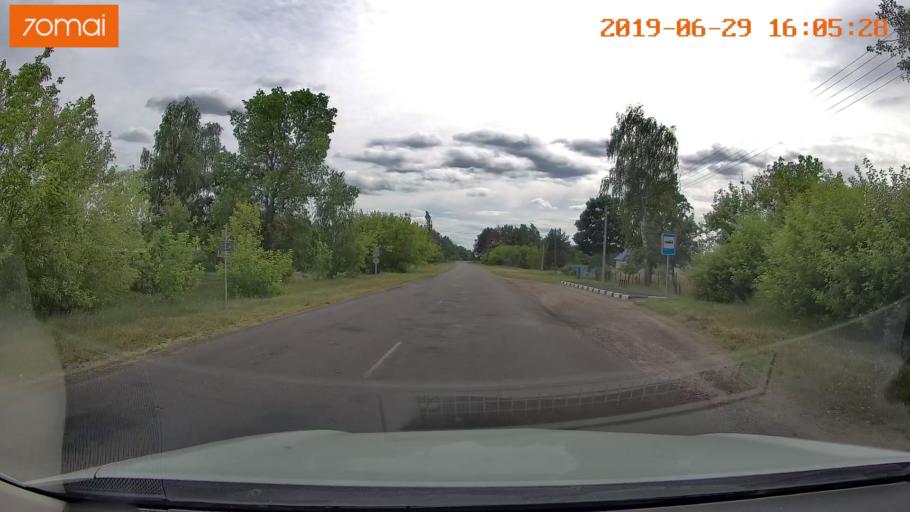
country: BY
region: Brest
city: Luninyets
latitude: 52.2164
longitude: 27.0193
